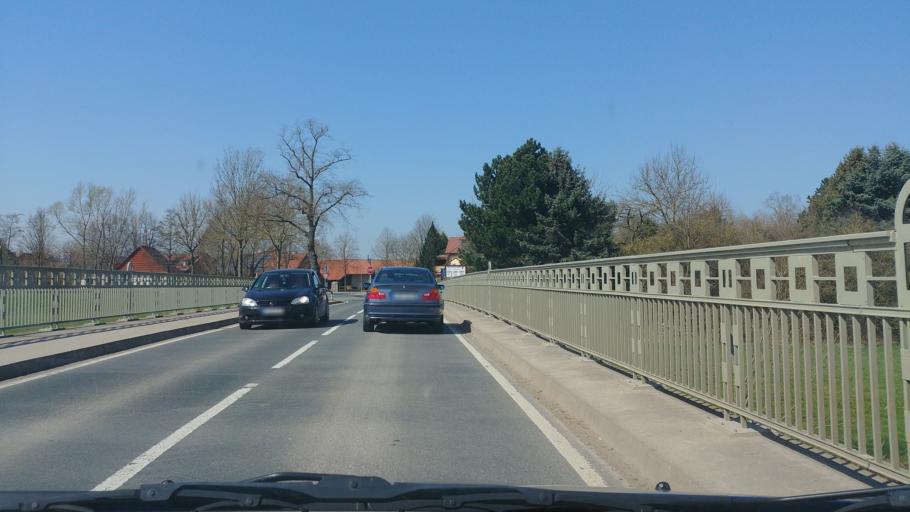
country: DE
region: Lower Saxony
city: Hillerse
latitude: 51.7382
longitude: 9.9503
